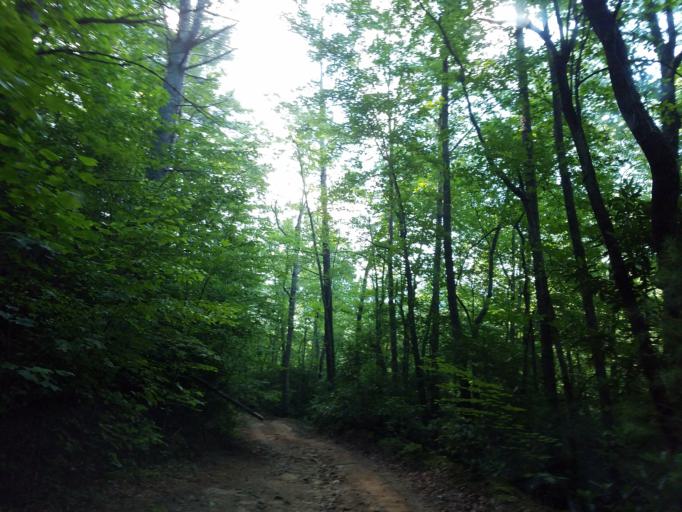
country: US
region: Georgia
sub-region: Dawson County
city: Dawsonville
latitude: 34.6242
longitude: -84.2357
